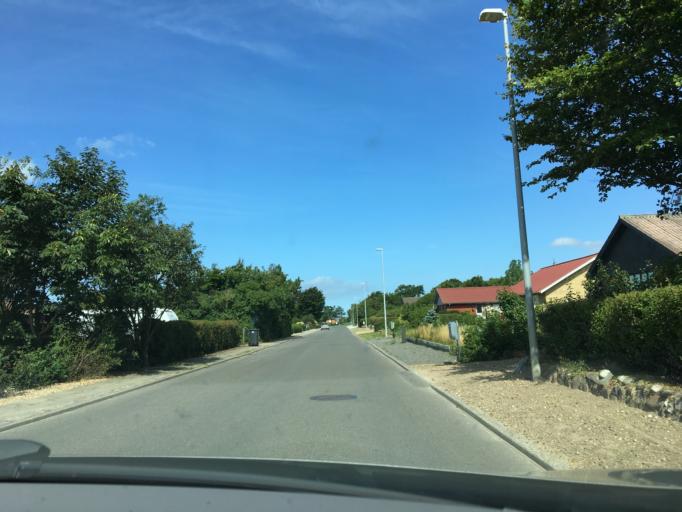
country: DK
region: Central Jutland
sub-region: Ringkobing-Skjern Kommune
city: Skjern
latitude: 55.9678
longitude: 8.3669
